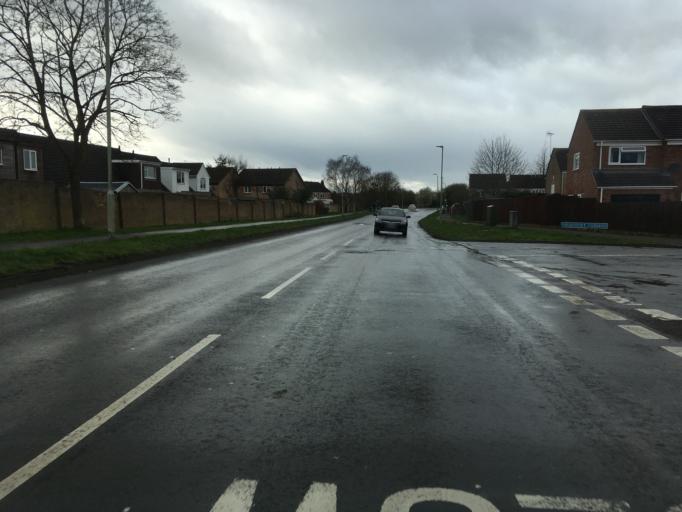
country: GB
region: England
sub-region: Gloucestershire
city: Gloucester
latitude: 51.8190
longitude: -2.2845
